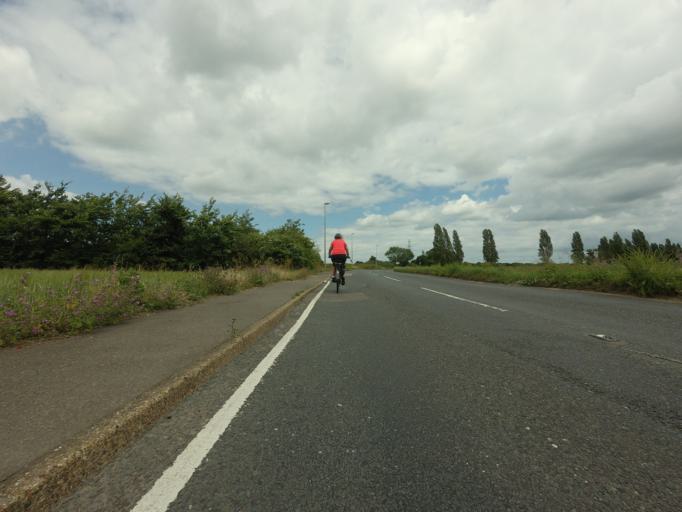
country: GB
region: England
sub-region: Kent
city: Queenborough
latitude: 51.4517
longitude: 0.7006
